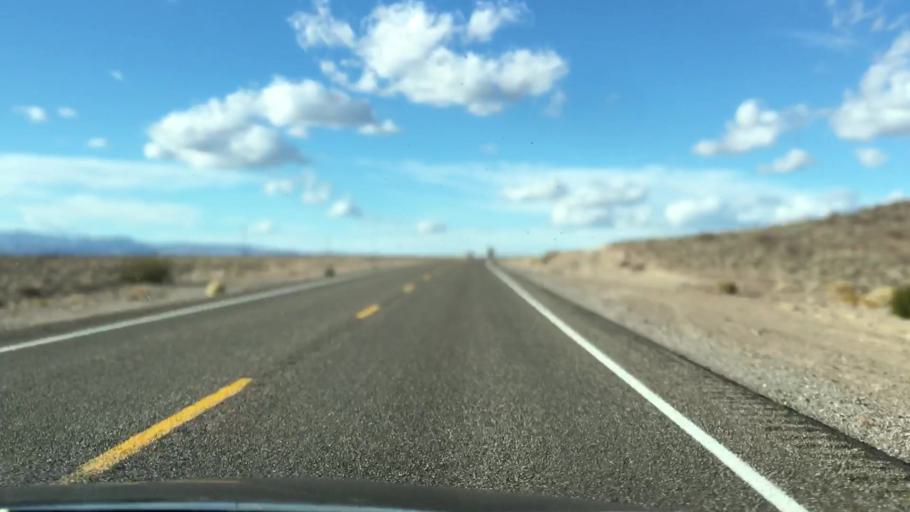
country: US
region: Nevada
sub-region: Nye County
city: Beatty
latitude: 37.1921
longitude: -116.9451
